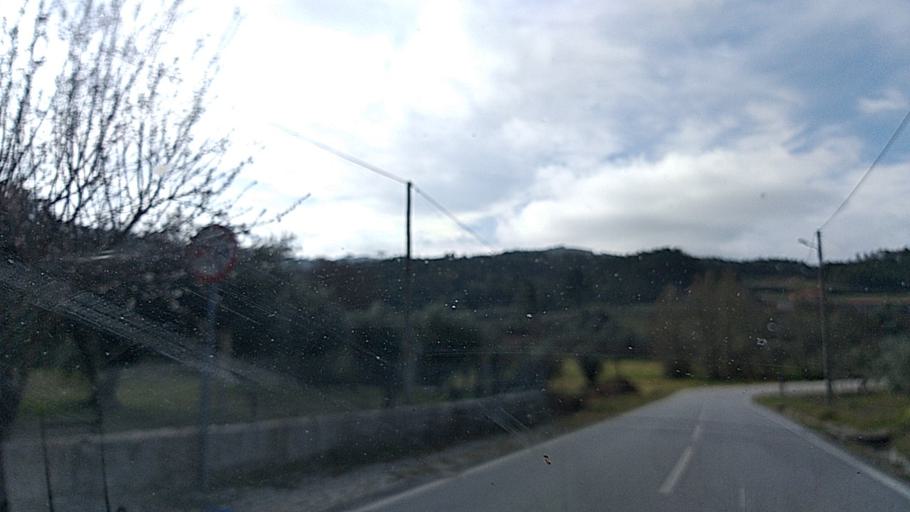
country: PT
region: Guarda
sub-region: Fornos de Algodres
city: Fornos de Algodres
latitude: 40.7026
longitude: -7.5592
